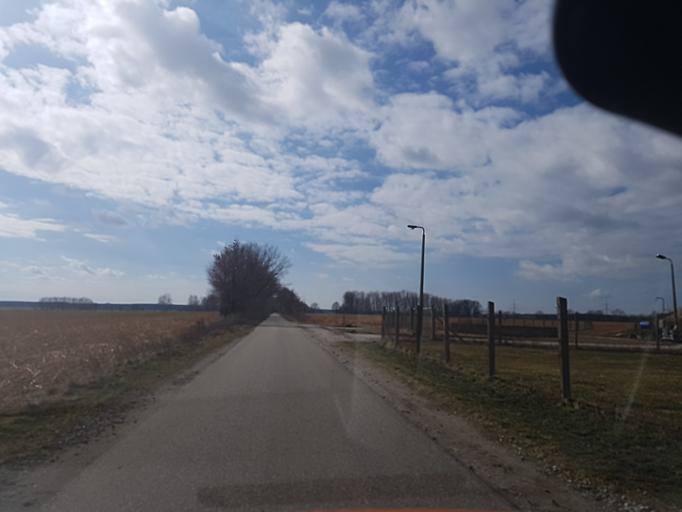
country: DE
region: Brandenburg
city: Ruckersdorf
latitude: 51.5865
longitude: 13.5384
